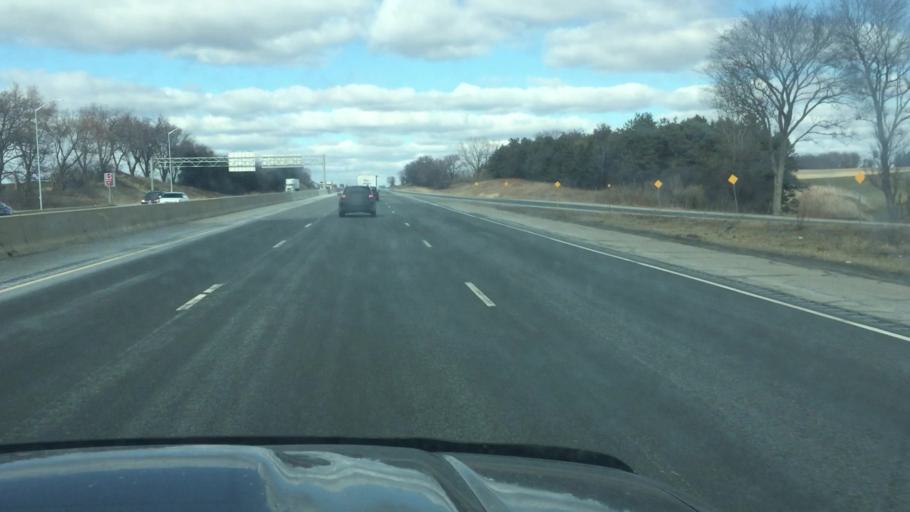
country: CA
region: Ontario
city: Ingersoll
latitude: 43.0289
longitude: -80.8520
